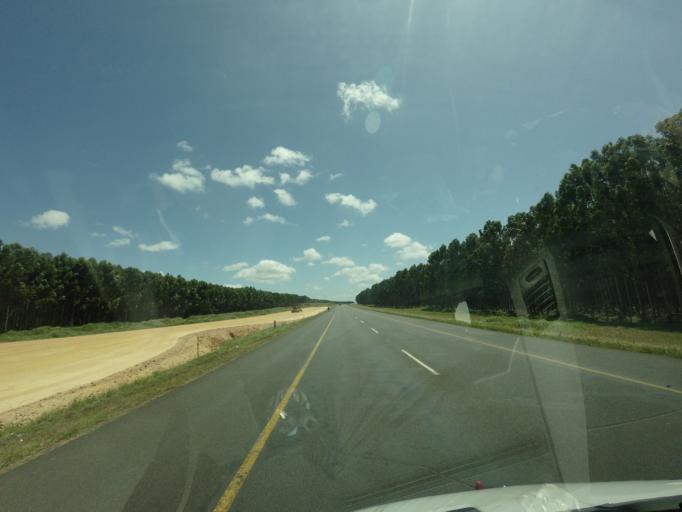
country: ZA
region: KwaZulu-Natal
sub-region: uThungulu District Municipality
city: Empangeni
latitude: -28.7424
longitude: 31.9385
